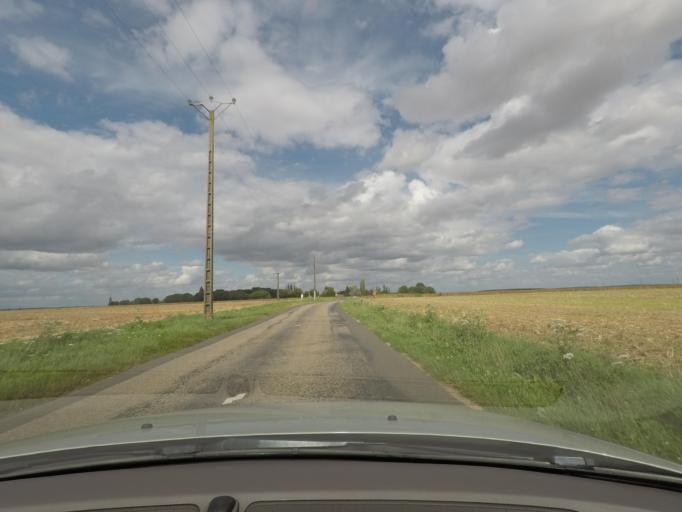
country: FR
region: Haute-Normandie
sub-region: Departement de l'Eure
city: Les Andelys
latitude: 49.1999
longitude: 1.4706
